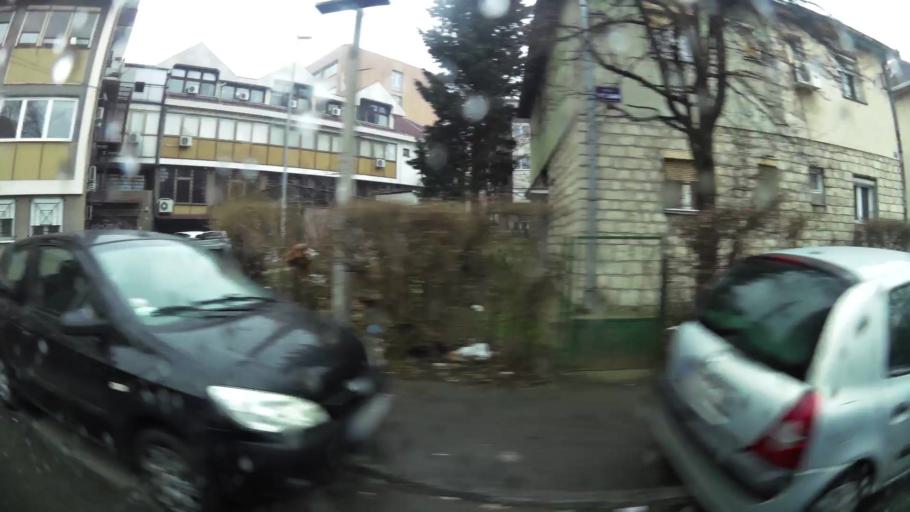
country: RS
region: Central Serbia
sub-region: Belgrade
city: Cukarica
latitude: 44.7819
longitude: 20.4154
